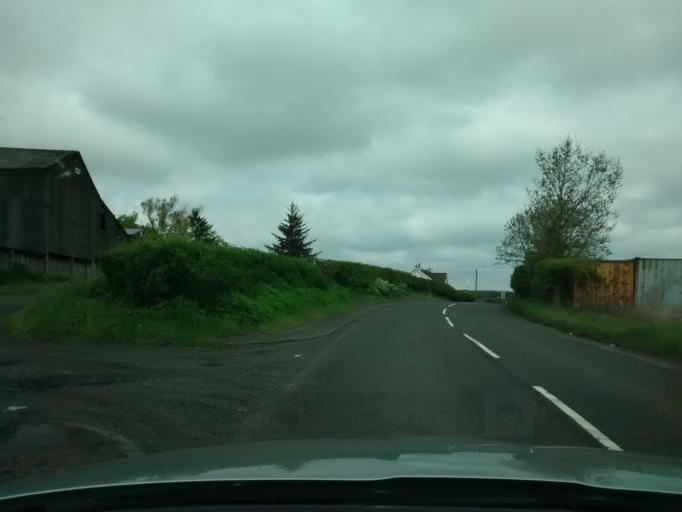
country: GB
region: Scotland
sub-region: North Lanarkshire
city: Harthill
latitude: 55.8738
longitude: -3.7560
